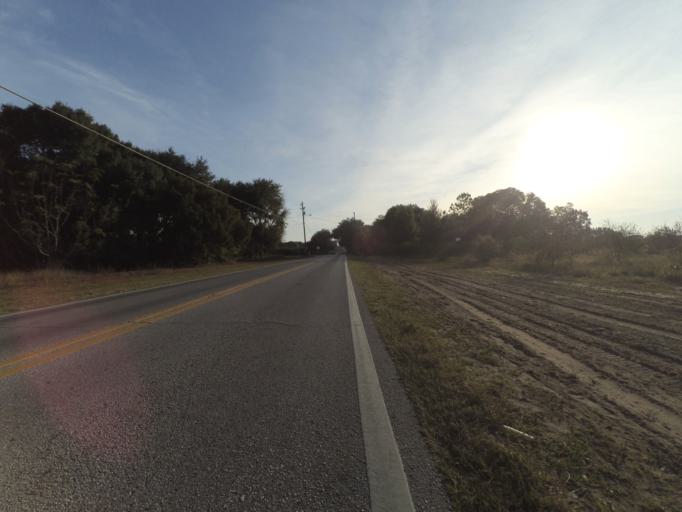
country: US
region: Florida
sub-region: Lake County
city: Umatilla
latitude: 28.9349
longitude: -81.6578
